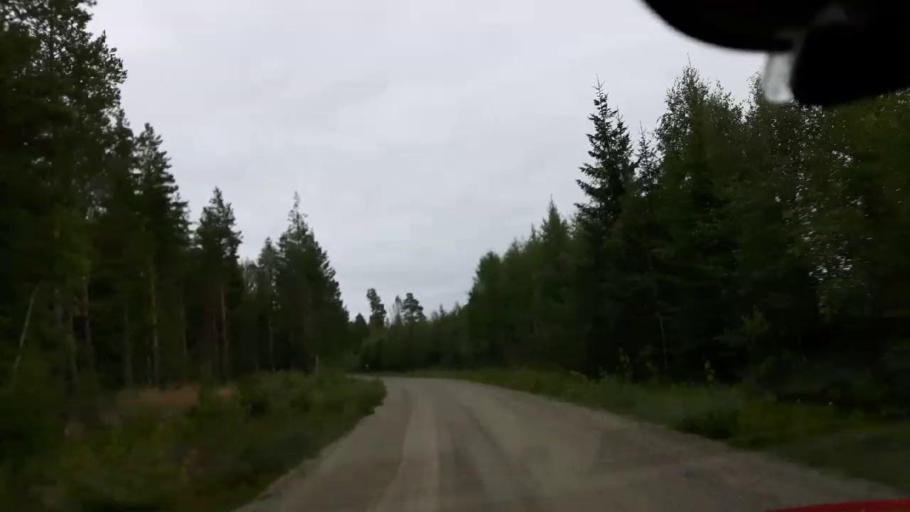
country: SE
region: Vaesternorrland
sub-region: Ange Kommun
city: Ange
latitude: 62.8039
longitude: 15.7509
